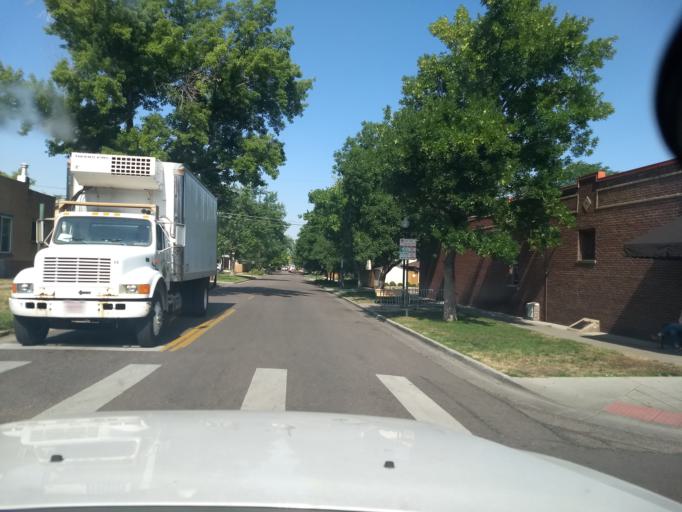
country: US
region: Colorado
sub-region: Arapahoe County
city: Englewood
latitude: 39.6876
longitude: -104.9805
